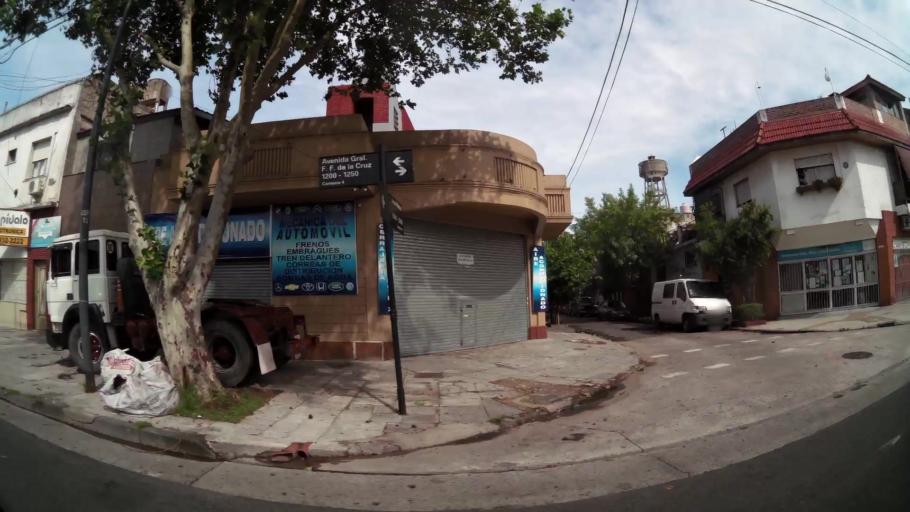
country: AR
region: Buenos Aires F.D.
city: Villa Lugano
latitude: -34.6460
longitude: -58.4264
